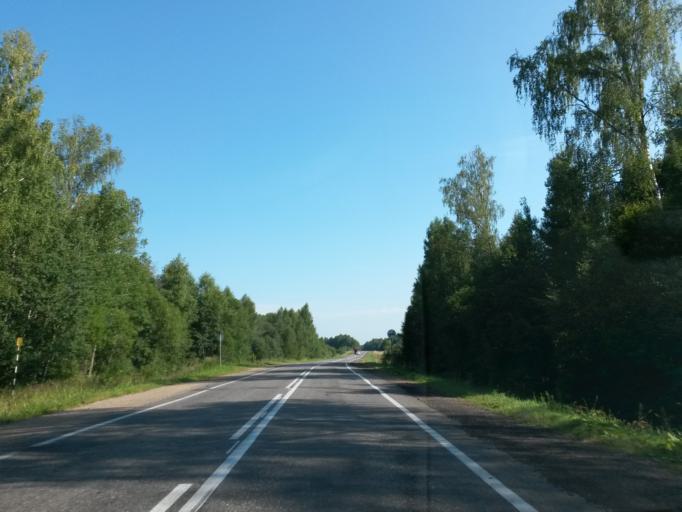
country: RU
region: Jaroslavl
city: Gavrilov-Yam
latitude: 57.3896
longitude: 39.9146
